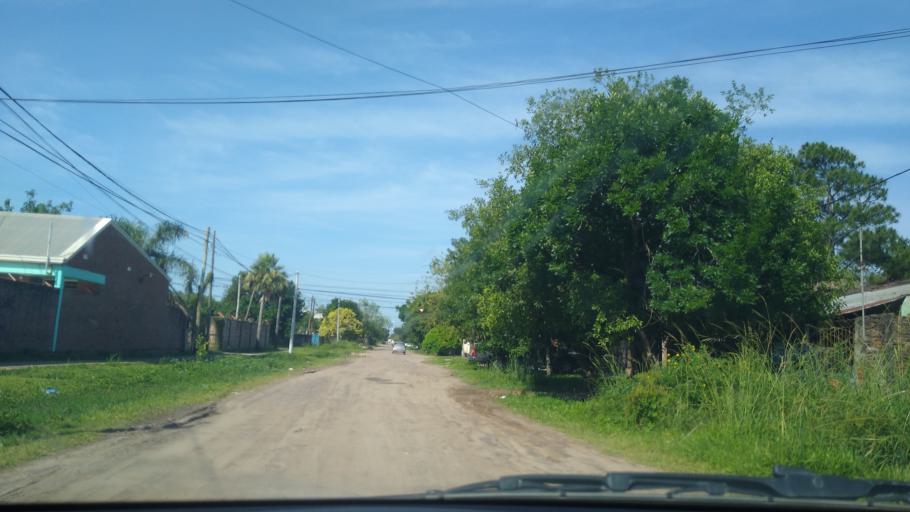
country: AR
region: Chaco
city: Barranqueras
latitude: -27.4891
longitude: -58.9483
